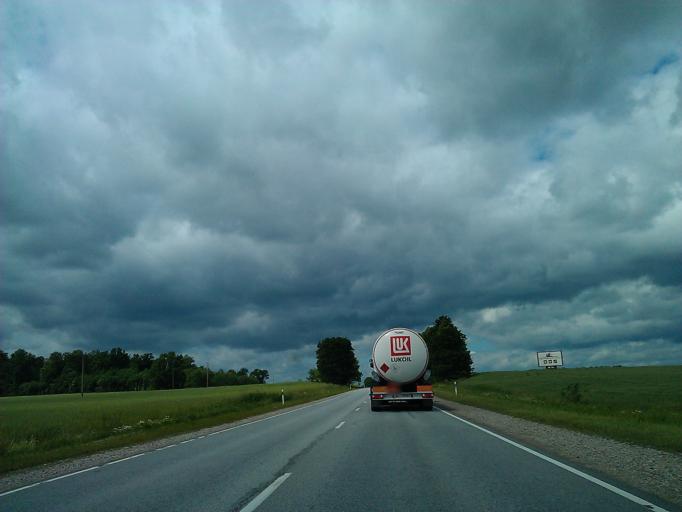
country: LV
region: Engure
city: Smarde
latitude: 56.9177
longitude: 23.3167
